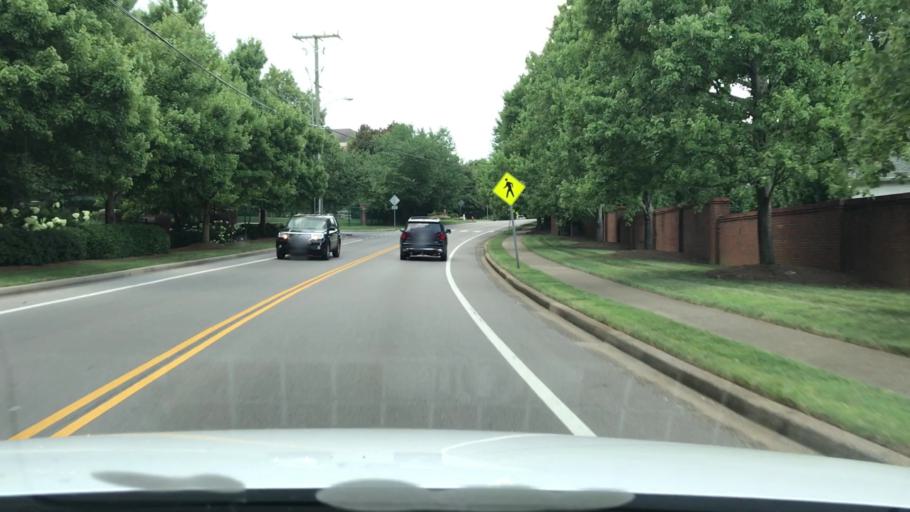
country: US
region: Tennessee
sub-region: Davidson County
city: Belle Meade
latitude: 36.1296
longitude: -86.8197
